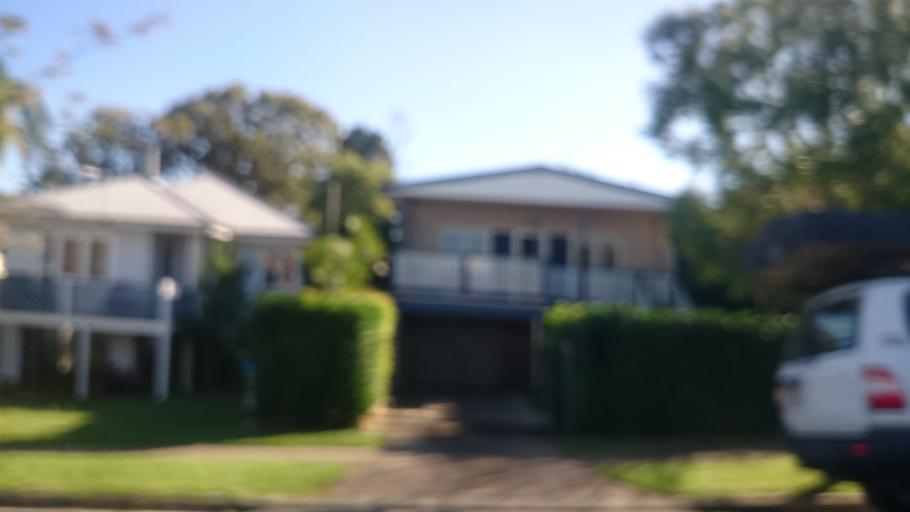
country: AU
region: Queensland
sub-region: Brisbane
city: Manly West
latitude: -27.4657
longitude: 153.1900
